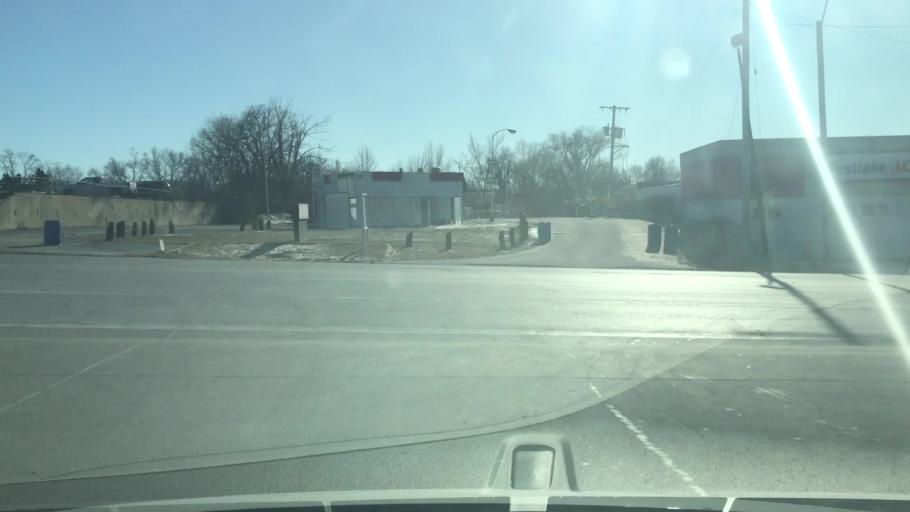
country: US
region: Missouri
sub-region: Clay County
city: Claycomo
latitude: 39.1882
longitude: -94.5204
